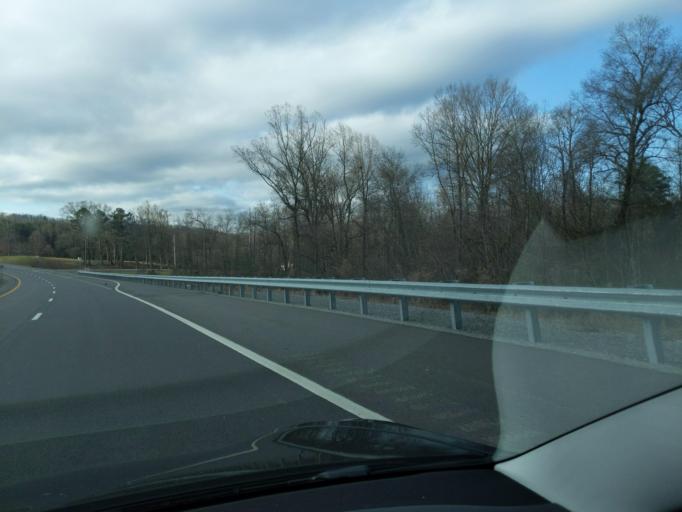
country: US
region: Tennessee
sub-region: Hamblen County
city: Morristown
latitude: 36.1620
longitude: -83.3450
